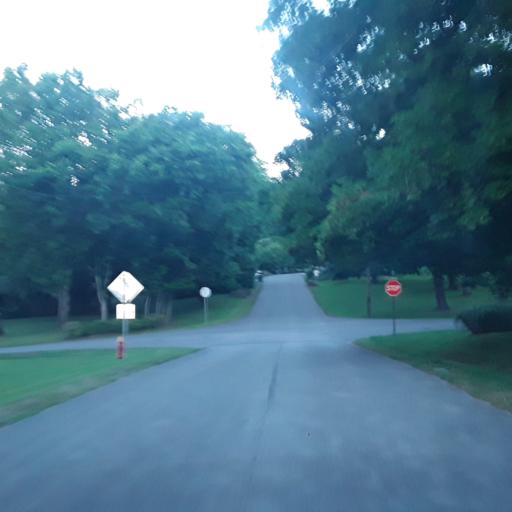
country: US
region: Tennessee
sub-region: Davidson County
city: Oak Hill
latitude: 36.0671
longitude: -86.7631
